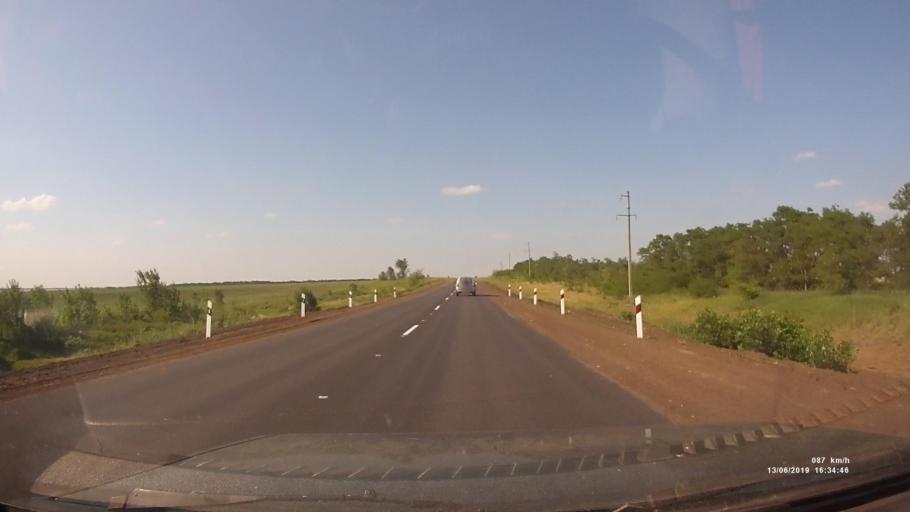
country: RU
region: Rostov
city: Kazanskaya
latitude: 49.8758
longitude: 41.2949
